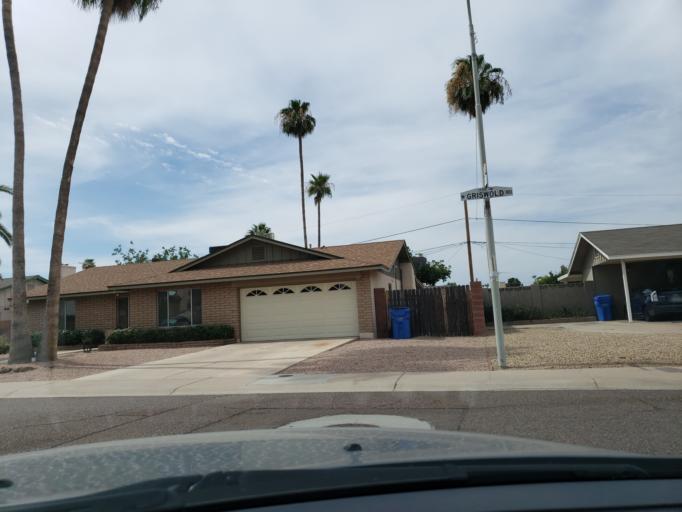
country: US
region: Arizona
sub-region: Maricopa County
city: Glendale
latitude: 33.5564
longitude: -112.0956
